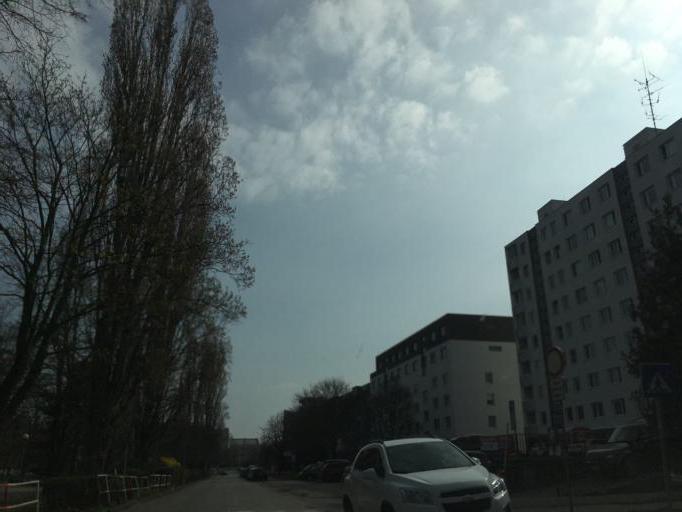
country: SK
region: Bratislavsky
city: Bratislava
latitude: 48.1563
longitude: 17.1592
